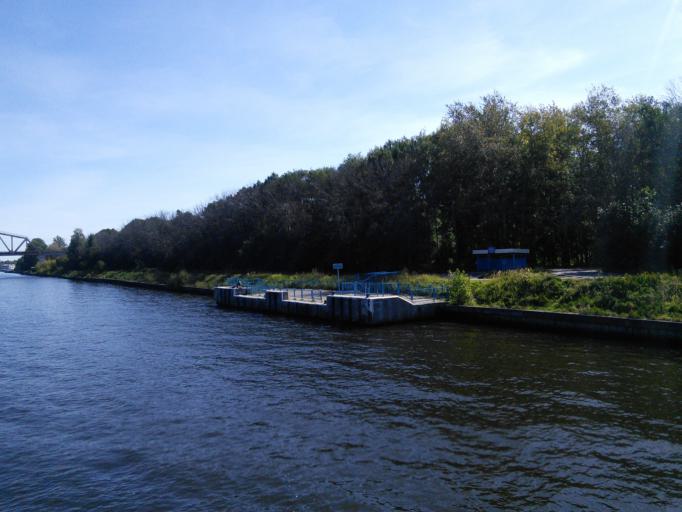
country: RU
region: Moskovskaya
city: Dolgoprudnyy
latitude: 55.9617
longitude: 37.5010
